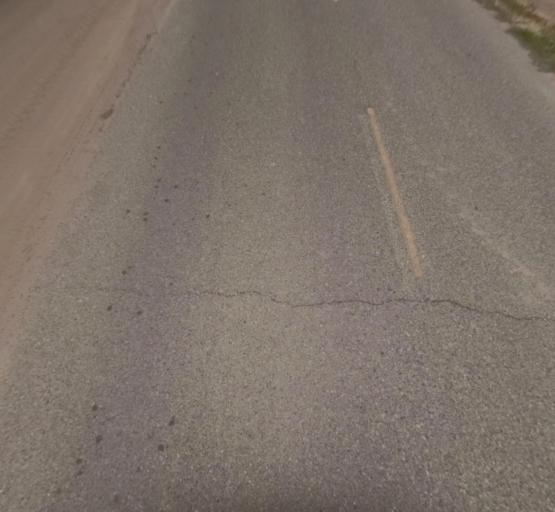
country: US
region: California
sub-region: Madera County
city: Madera
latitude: 36.9249
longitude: -120.1561
